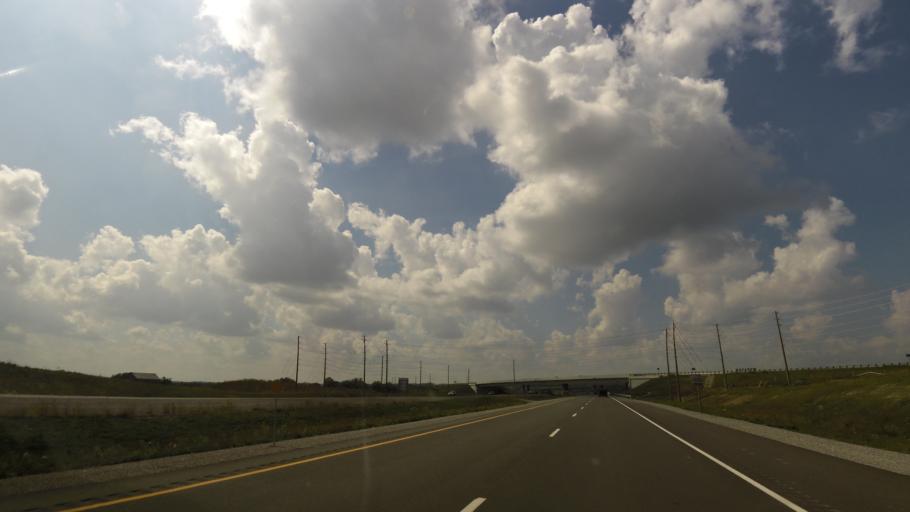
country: CA
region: Ontario
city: Ajax
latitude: 43.9493
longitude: -78.9733
